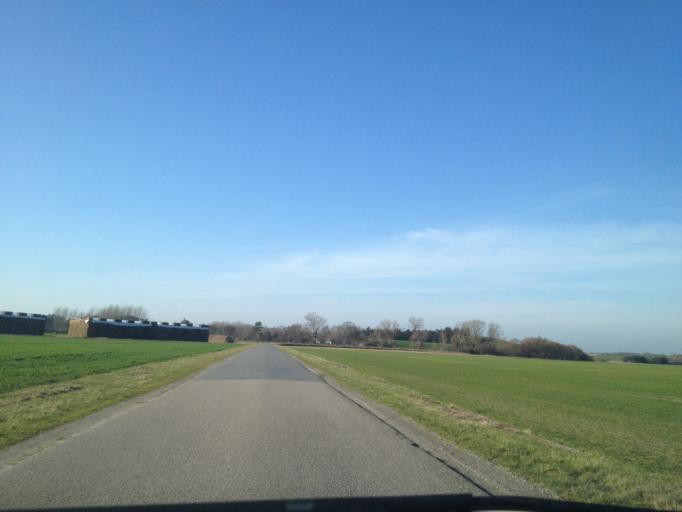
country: DK
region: South Denmark
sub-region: Kerteminde Kommune
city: Kerteminde
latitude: 55.5494
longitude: 10.6322
